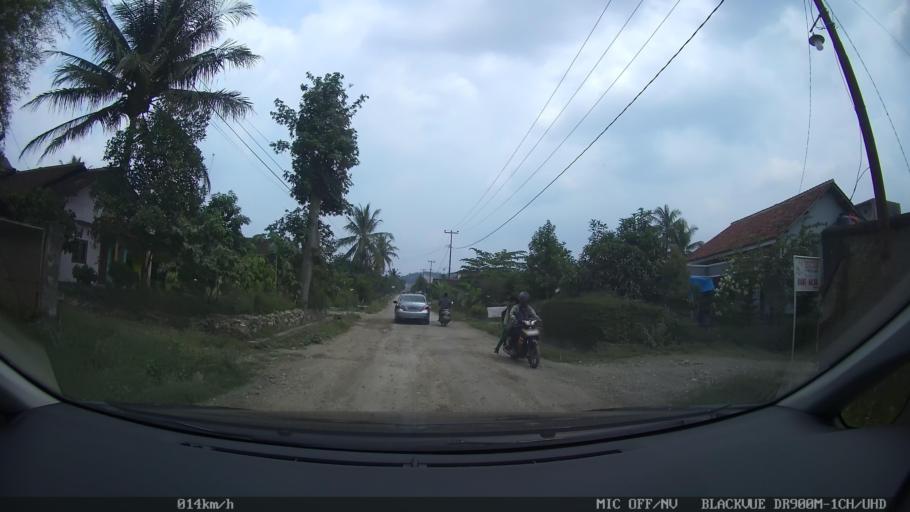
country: ID
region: Lampung
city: Gadingrejo
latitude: -5.3749
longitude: 105.0304
